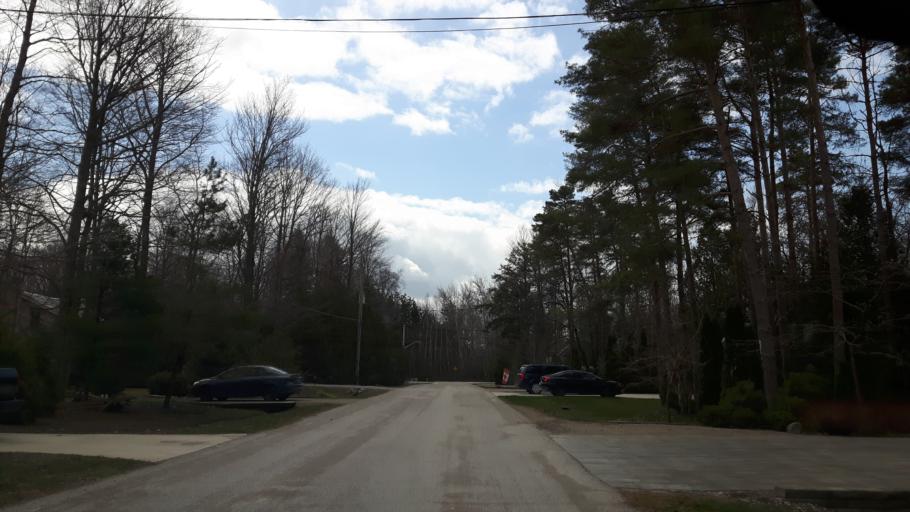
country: CA
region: Ontario
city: Bluewater
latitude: 43.5553
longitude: -81.6974
